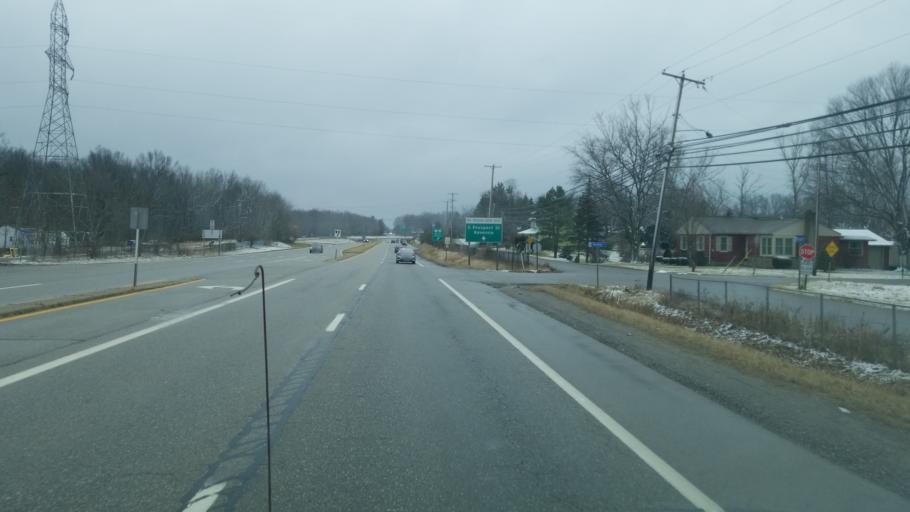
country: US
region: Ohio
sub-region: Portage County
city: Ravenna
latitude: 41.1128
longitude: -81.2423
